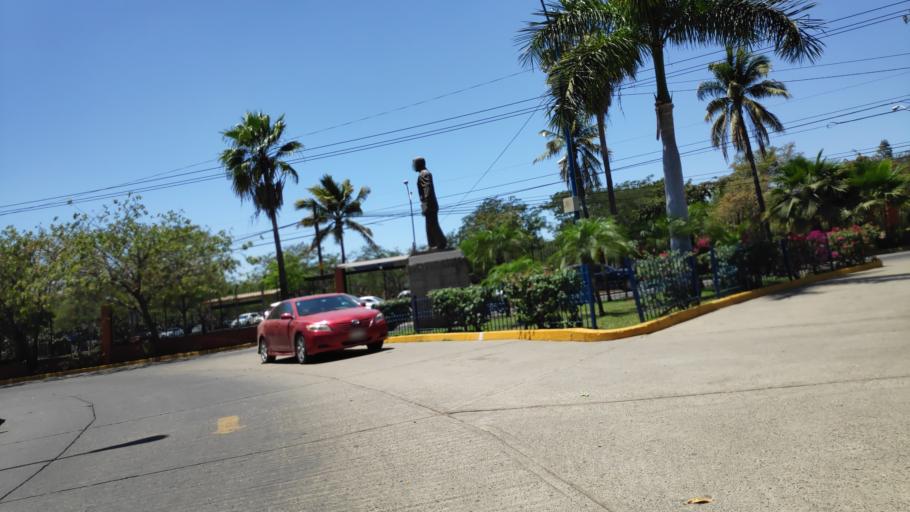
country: MX
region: Sinaloa
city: Culiacan
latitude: 24.8253
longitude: -107.3833
